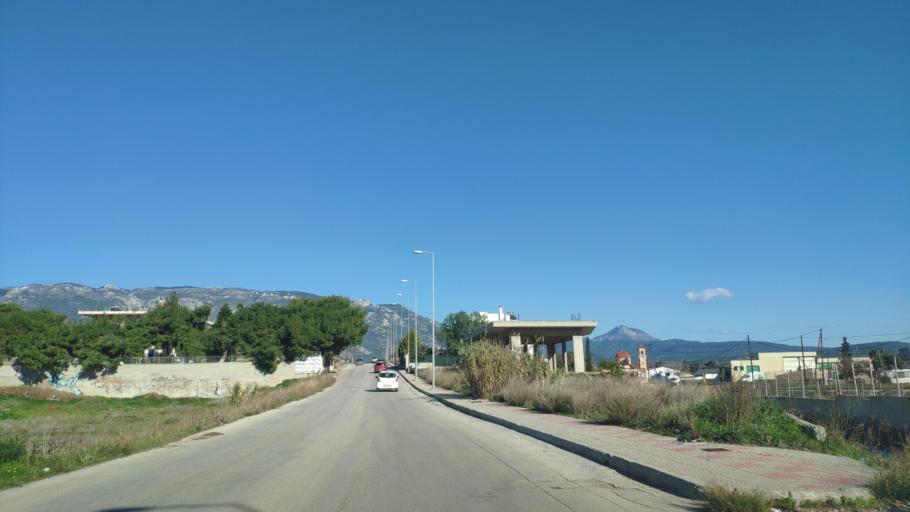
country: GR
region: Peloponnese
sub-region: Nomos Korinthias
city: Korinthos
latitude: 37.9432
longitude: 22.9535
